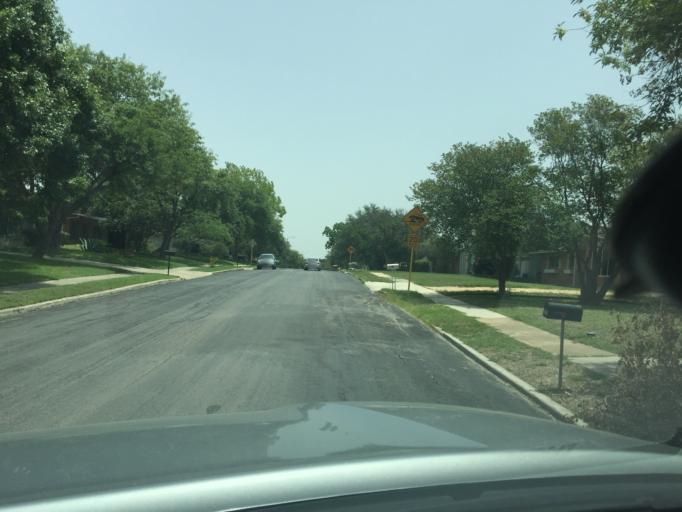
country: US
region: Texas
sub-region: Bexar County
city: Castle Hills
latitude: 29.5226
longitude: -98.4916
